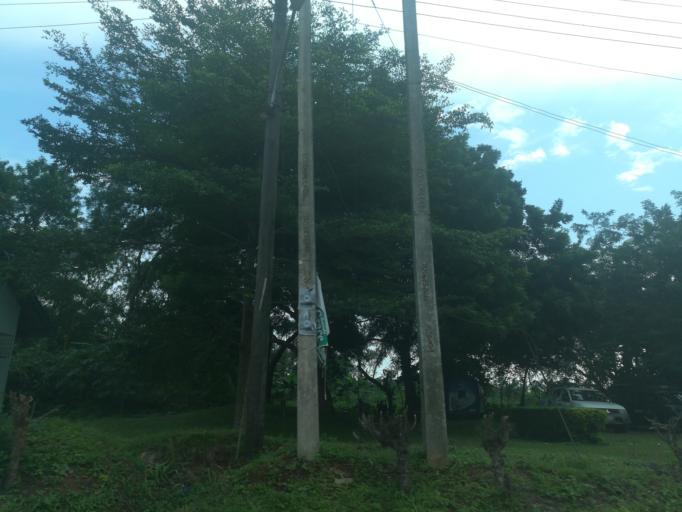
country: NG
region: Lagos
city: Ikorodu
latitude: 6.6454
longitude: 3.5203
